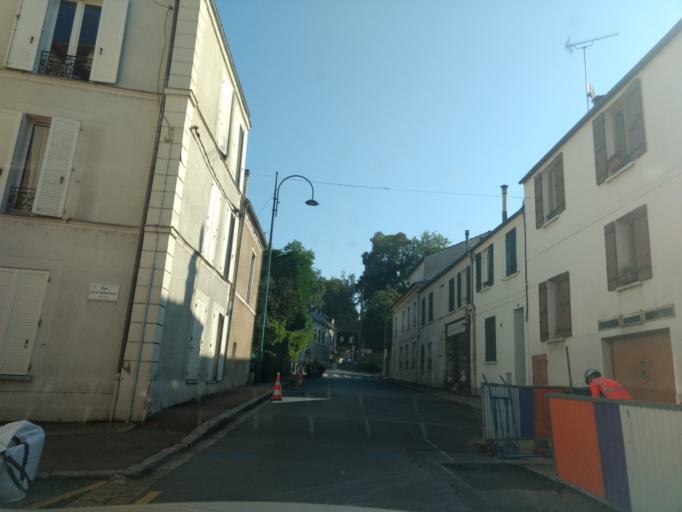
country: FR
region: Ile-de-France
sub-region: Departement des Yvelines
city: Jouy-en-Josas
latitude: 48.7658
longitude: 2.1695
